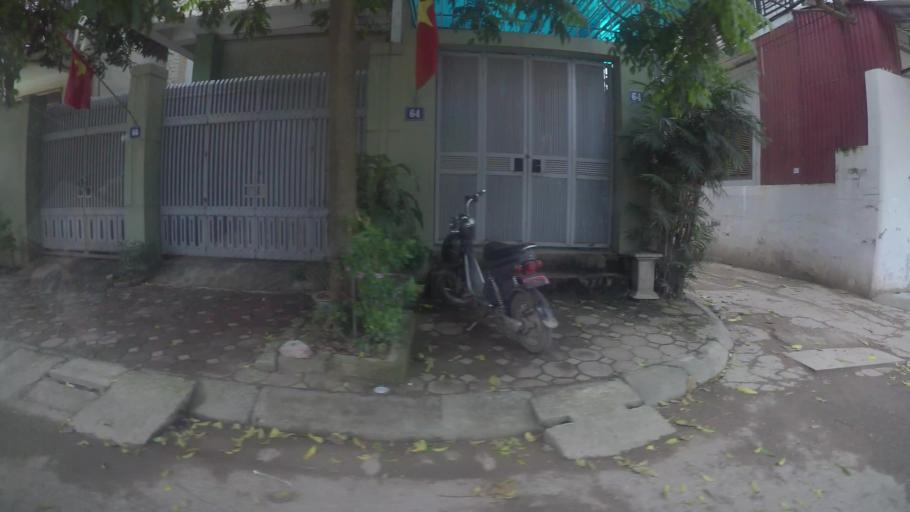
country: VN
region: Ha Noi
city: Tay Ho
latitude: 21.0870
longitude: 105.7956
